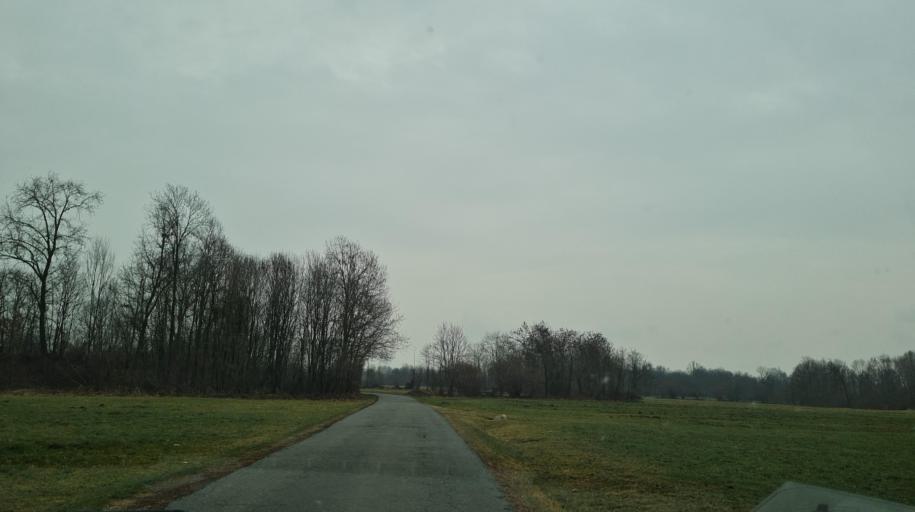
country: IT
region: Piedmont
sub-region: Provincia di Biella
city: Ceresane-Curanuova
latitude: 45.5168
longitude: 8.0154
